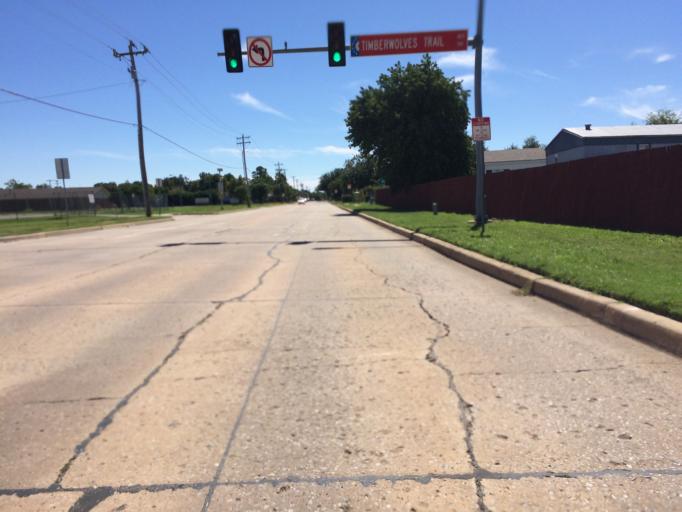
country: US
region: Oklahoma
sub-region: Cleveland County
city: Norman
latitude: 35.2395
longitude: -97.4501
